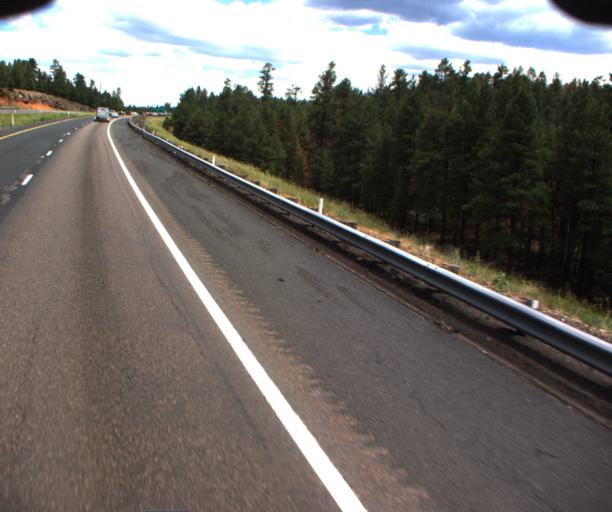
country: US
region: Arizona
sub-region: Coconino County
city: Mountainaire
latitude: 35.0431
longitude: -111.6850
